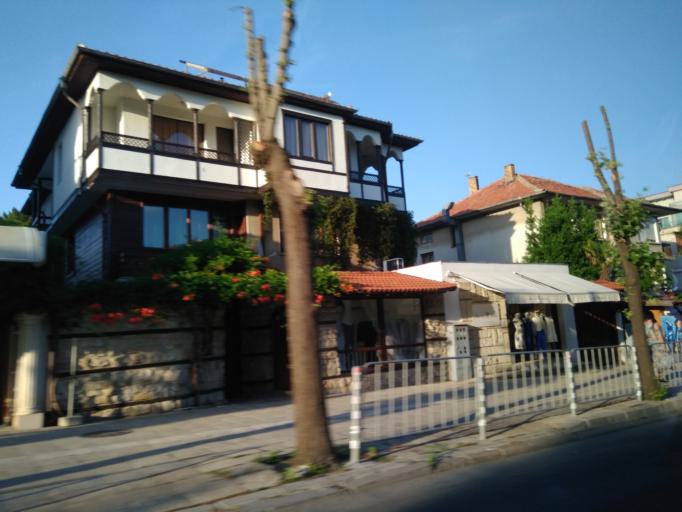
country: BG
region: Burgas
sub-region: Obshtina Nesebur
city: Nesebar
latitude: 42.6617
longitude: 27.7213
